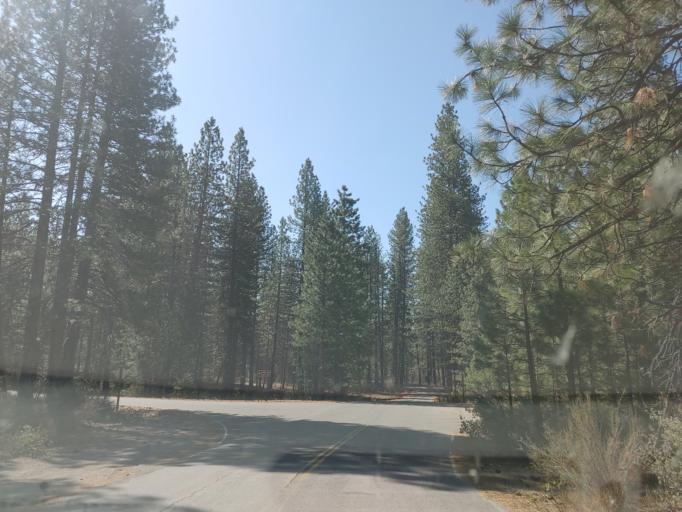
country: US
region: California
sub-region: Siskiyou County
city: McCloud
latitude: 41.2492
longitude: -122.0265
